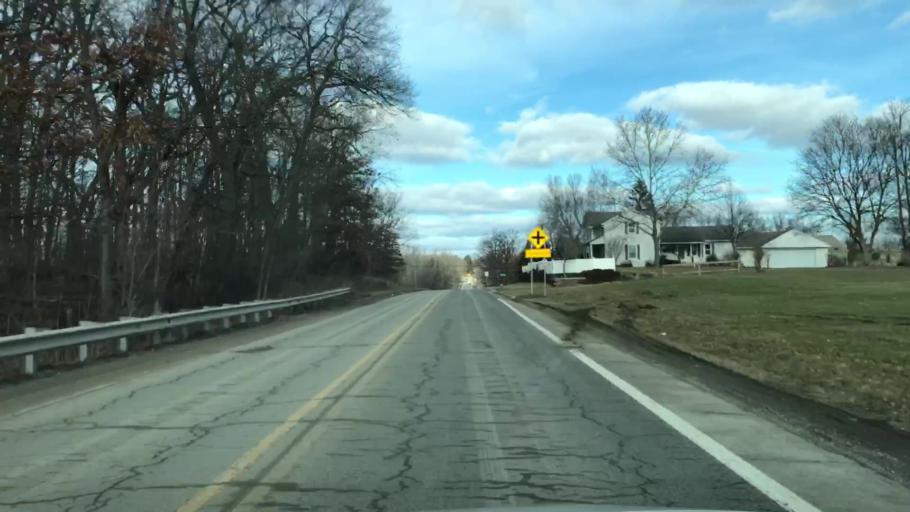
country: US
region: Michigan
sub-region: Oakland County
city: Lake Orion
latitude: 42.7652
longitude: -83.1979
